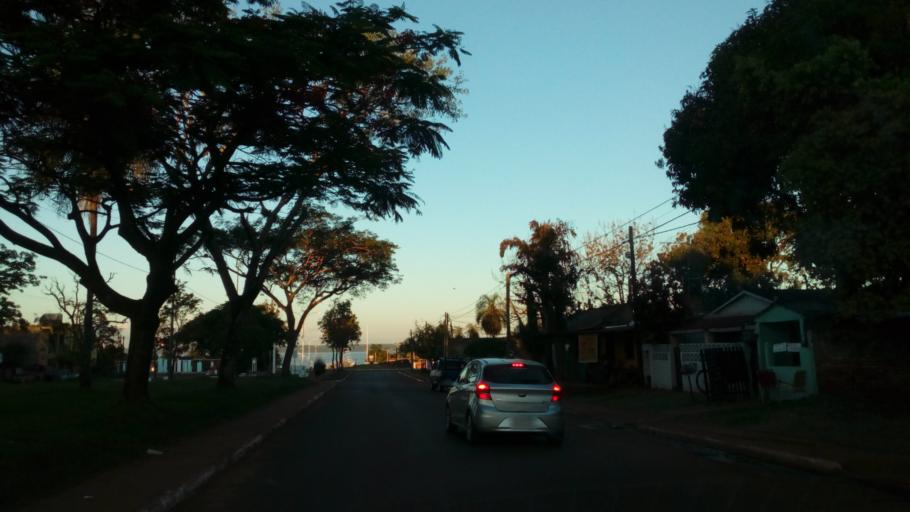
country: AR
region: Misiones
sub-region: Departamento de Capital
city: Posadas
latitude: -27.4293
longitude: -55.8808
